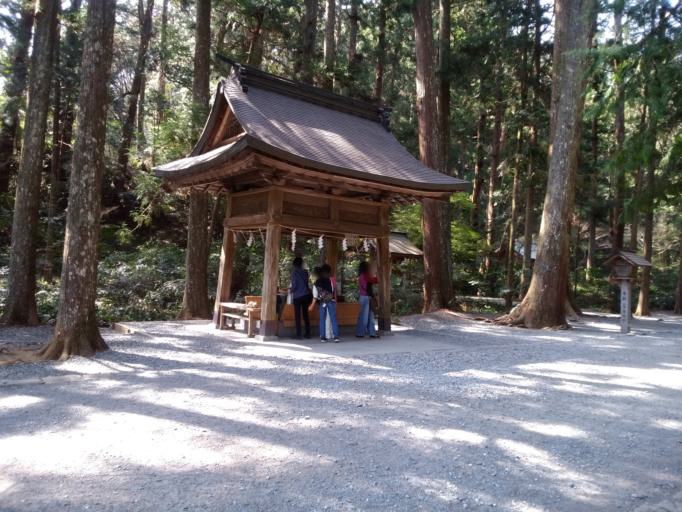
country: JP
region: Shizuoka
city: Mori
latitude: 34.8453
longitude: 137.9000
